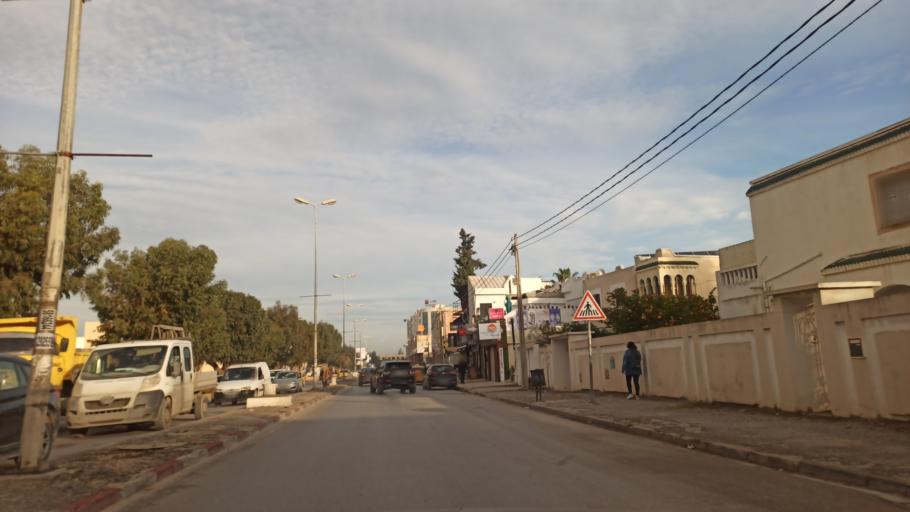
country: TN
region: Tunis
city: La Goulette
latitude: 36.8561
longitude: 10.2569
